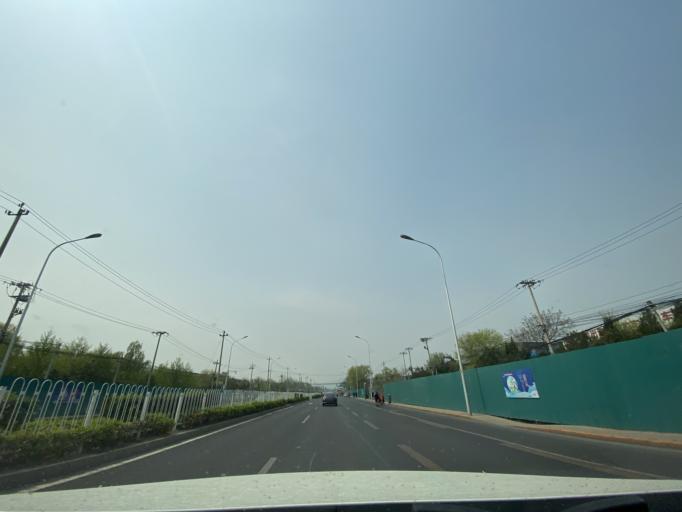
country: CN
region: Beijing
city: Sijiqing
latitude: 39.9456
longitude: 116.2535
